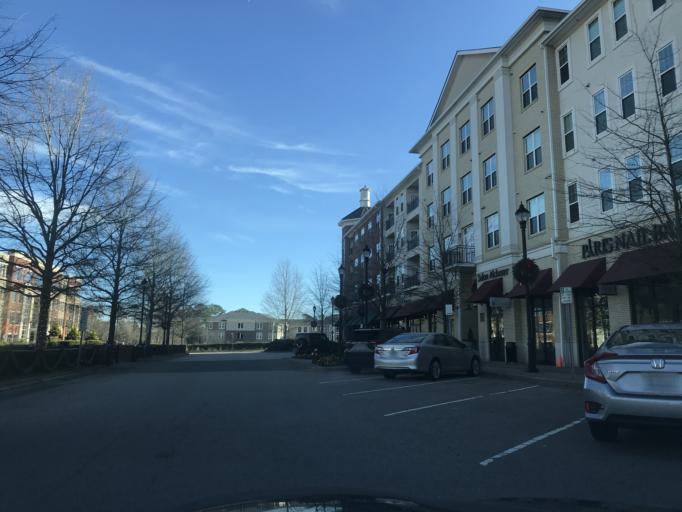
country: US
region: North Carolina
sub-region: Wake County
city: Cary
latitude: 35.8074
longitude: -78.7304
